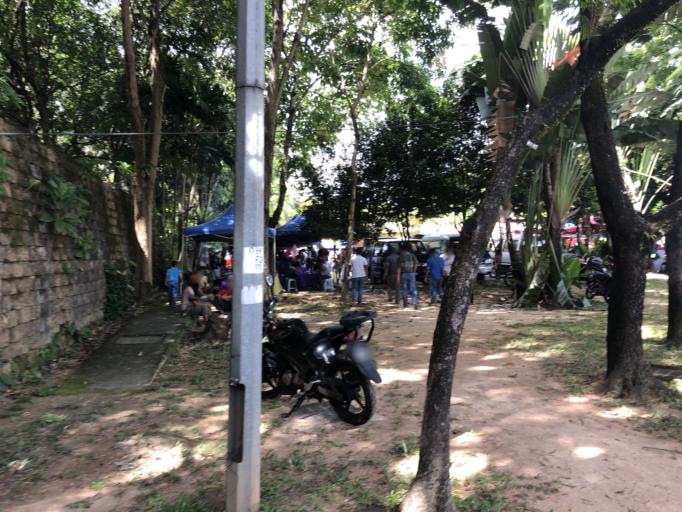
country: MY
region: Kuala Lumpur
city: Kuala Lumpur
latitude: 3.1732
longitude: 101.6724
